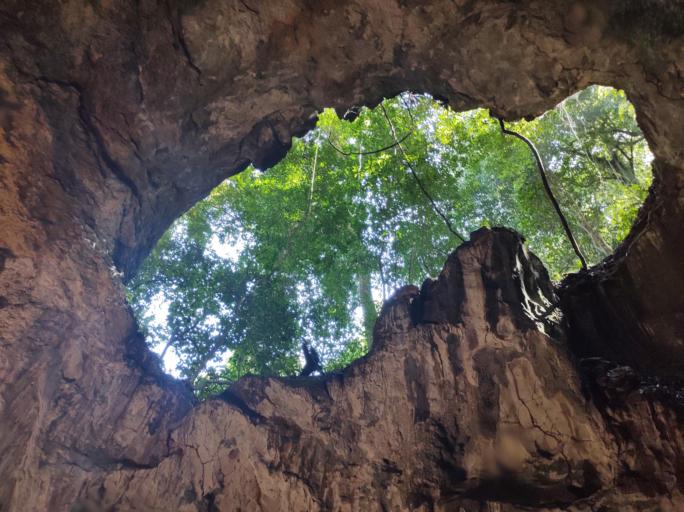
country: DO
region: Hato Mayor
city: Sabana de La Mar
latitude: 19.0775
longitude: -69.4666
